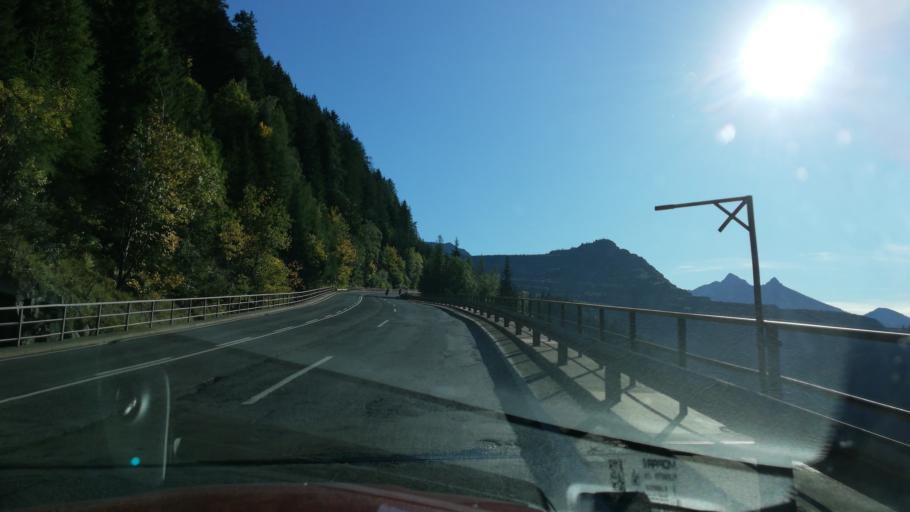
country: AT
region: Styria
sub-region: Politischer Bezirk Leoben
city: Eisenerz
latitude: 47.5458
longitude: 14.9313
